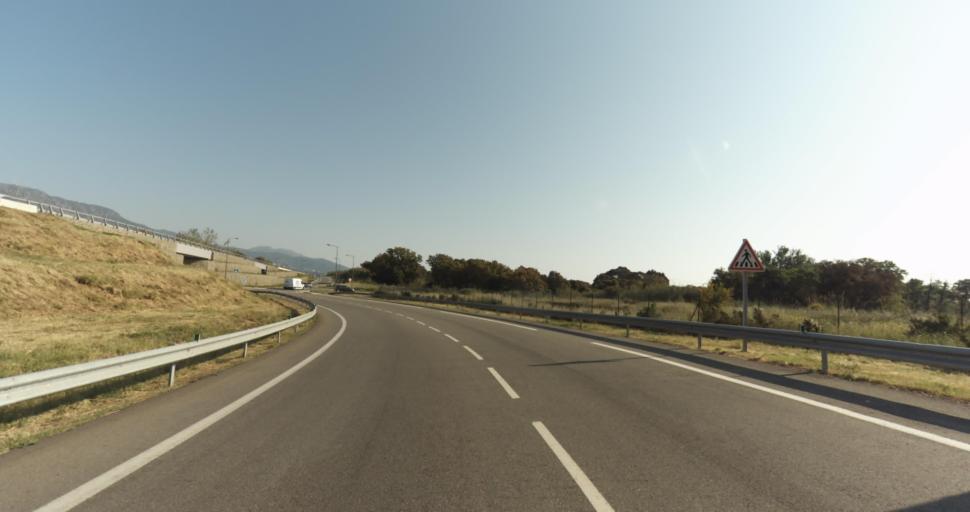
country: FR
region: Corsica
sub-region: Departement de la Haute-Corse
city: Biguglia
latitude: 42.6402
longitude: 9.4399
